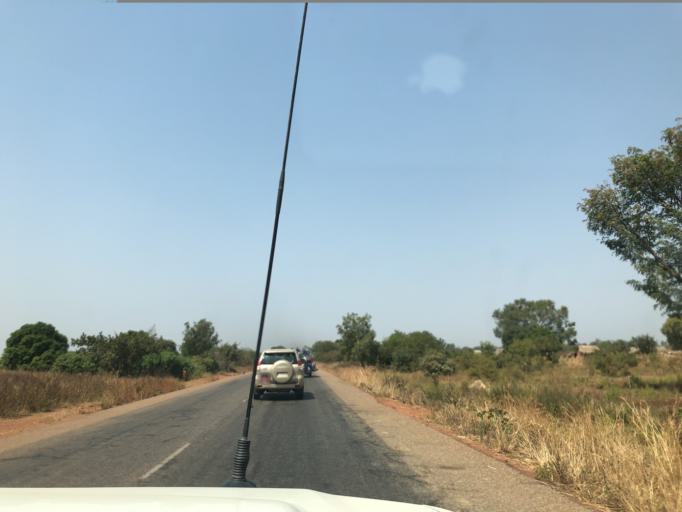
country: TD
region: Tandjile
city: Kelo
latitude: 8.9086
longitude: 15.8451
